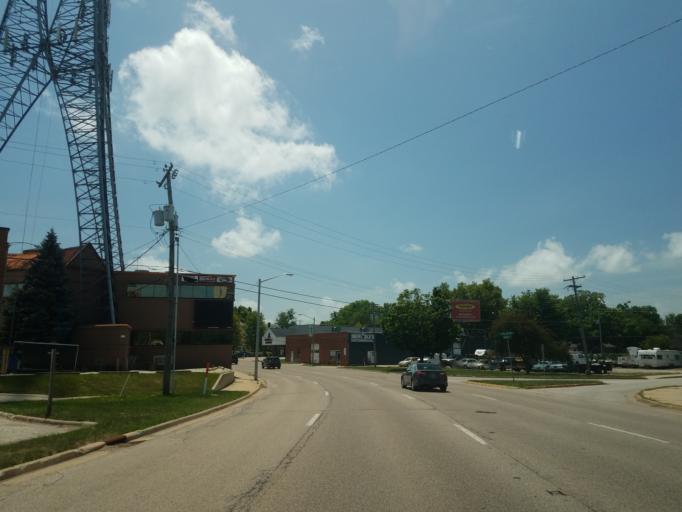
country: US
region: Illinois
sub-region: McLean County
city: Bloomington
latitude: 40.4836
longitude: -88.9952
